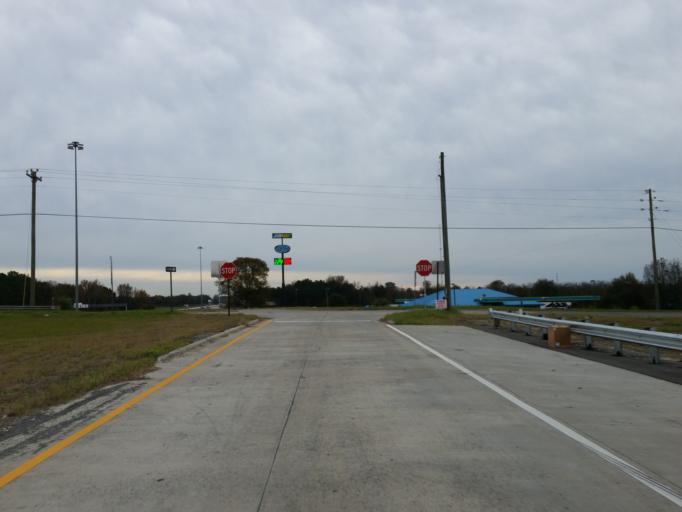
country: US
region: Georgia
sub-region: Dooly County
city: Unadilla
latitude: 32.1922
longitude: -83.7483
